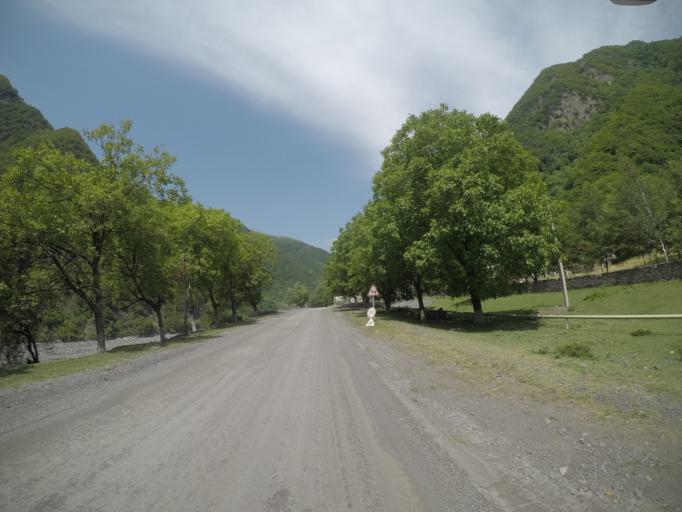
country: AZ
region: Qakh Rayon
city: Qaxbas
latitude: 41.4610
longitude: 47.0295
